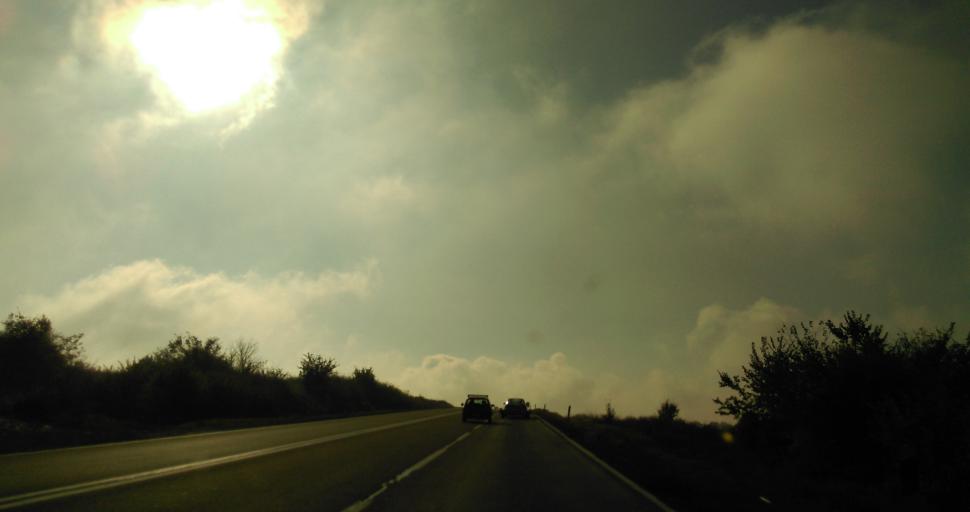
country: RS
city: Rusanj
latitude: 44.6620
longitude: 20.4285
